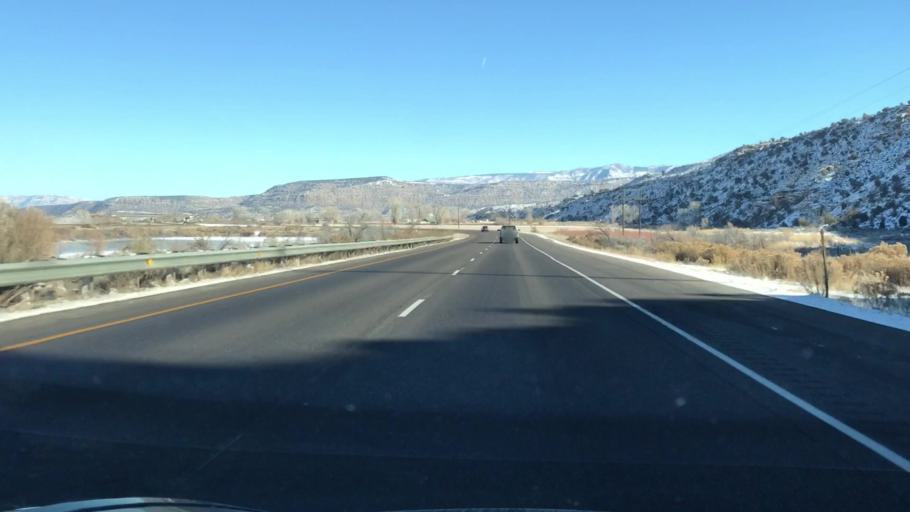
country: US
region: Colorado
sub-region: Mesa County
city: Palisade
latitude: 39.2804
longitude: -108.2356
